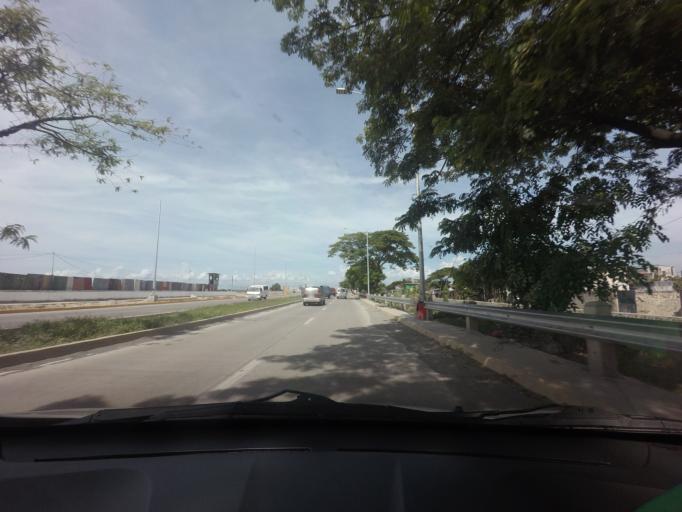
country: PH
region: Calabarzon
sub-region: Province of Rizal
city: Taguig
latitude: 14.5336
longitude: 121.0998
